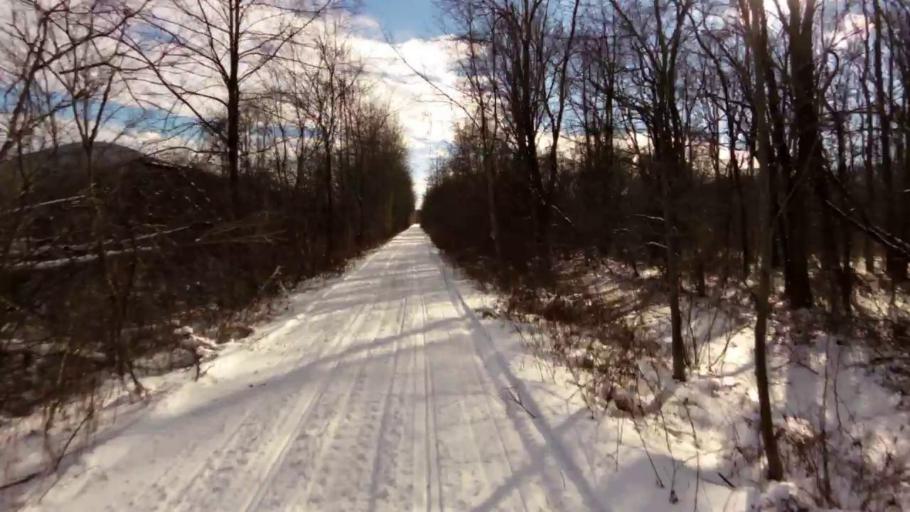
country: US
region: Pennsylvania
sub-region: McKean County
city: Foster Brook
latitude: 42.0299
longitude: -78.6321
